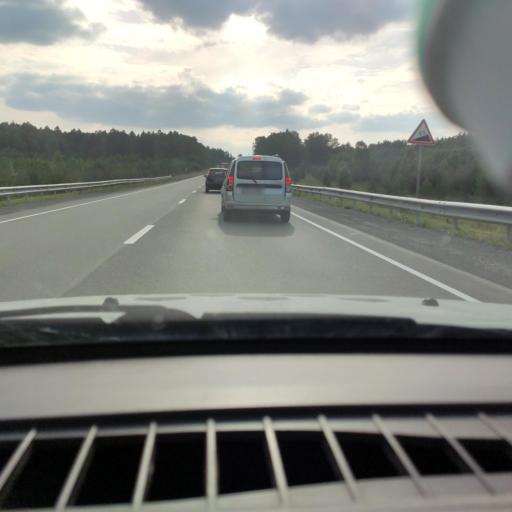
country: RU
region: Sverdlovsk
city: Bisert'
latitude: 56.8335
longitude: 58.8362
